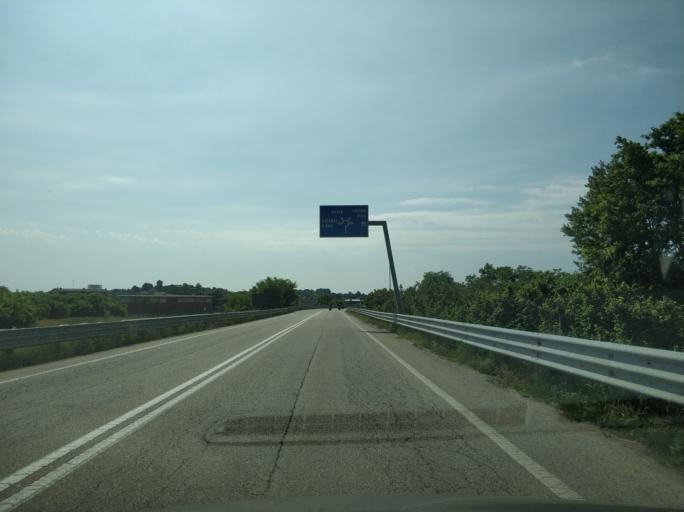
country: IT
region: Piedmont
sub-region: Provincia di Cuneo
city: Monta
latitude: 44.8231
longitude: 7.9449
